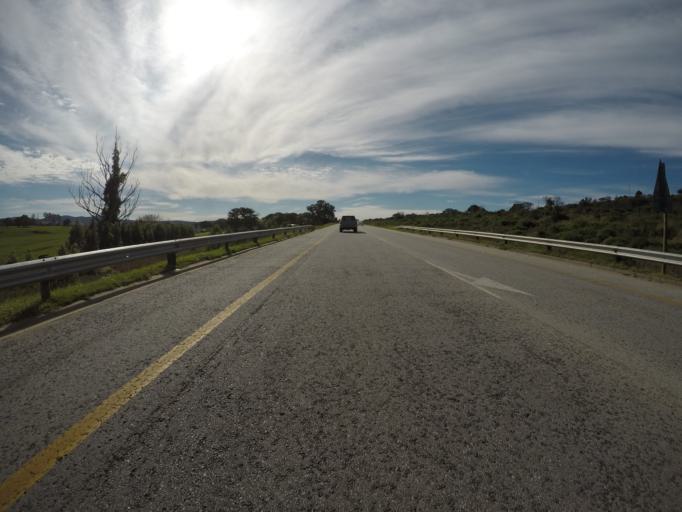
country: ZA
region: Eastern Cape
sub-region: Cacadu District Municipality
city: Jeffrey's Bay
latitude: -33.9006
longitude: 25.1146
